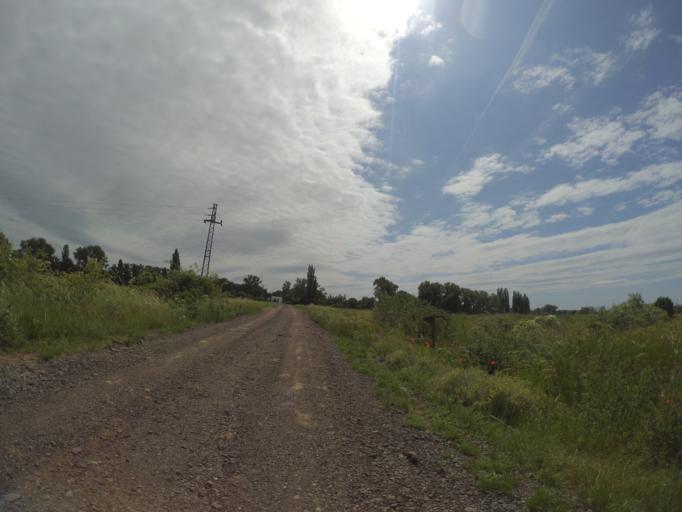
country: CZ
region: Central Bohemia
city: Lysa nad Labem
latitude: 50.1834
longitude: 14.8382
